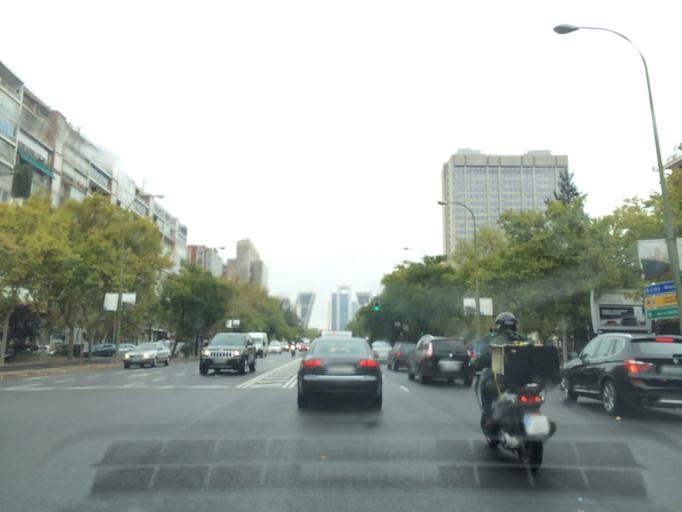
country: ES
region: Madrid
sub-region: Provincia de Madrid
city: Chamartin
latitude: 40.4557
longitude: -3.6903
